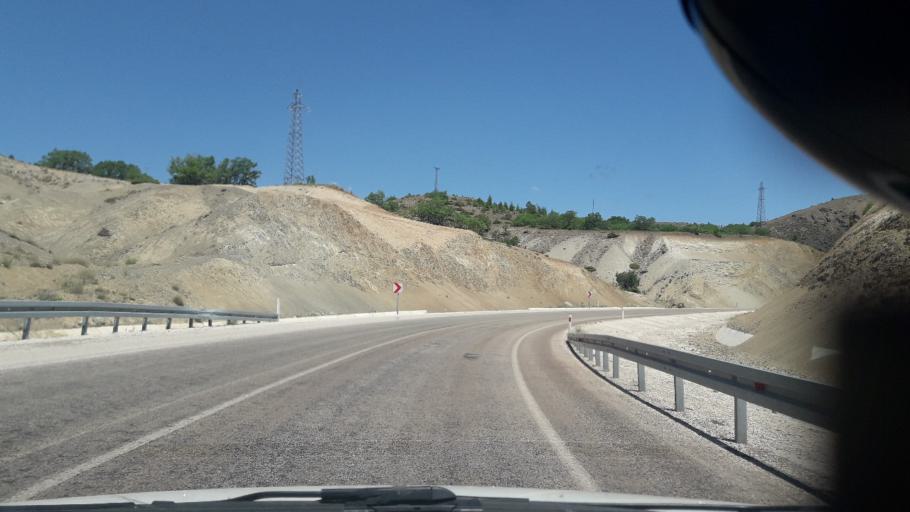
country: TR
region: Malatya
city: Hekimhan
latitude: 38.8300
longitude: 37.8650
